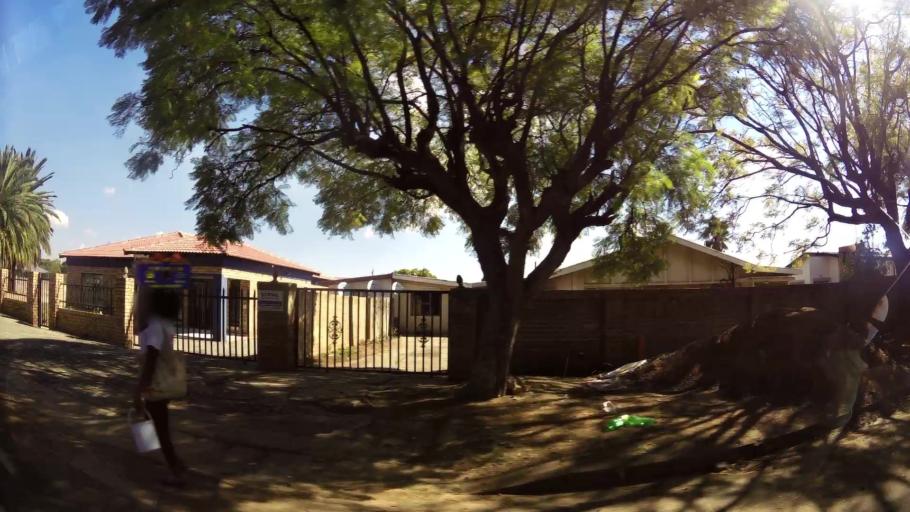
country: ZA
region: Mpumalanga
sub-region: Nkangala District Municipality
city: Witbank
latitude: -25.8815
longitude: 29.2253
